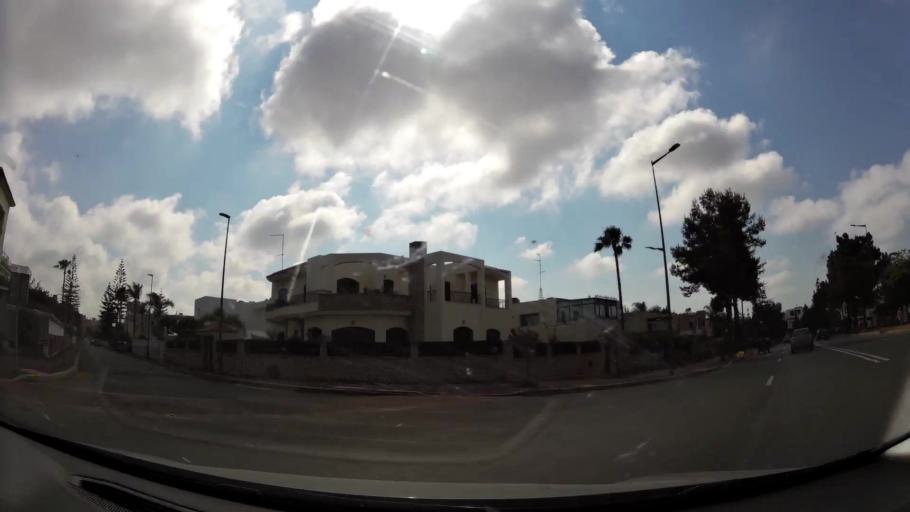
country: MA
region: Rabat-Sale-Zemmour-Zaer
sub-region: Skhirate-Temara
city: Temara
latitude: 33.9589
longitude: -6.8614
